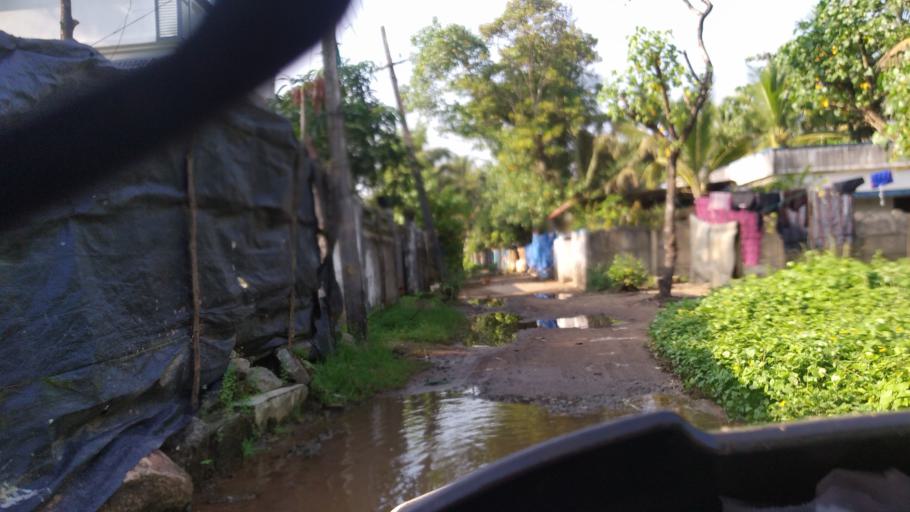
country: IN
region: Kerala
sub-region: Ernakulam
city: Cochin
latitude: 9.9882
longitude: 76.2256
